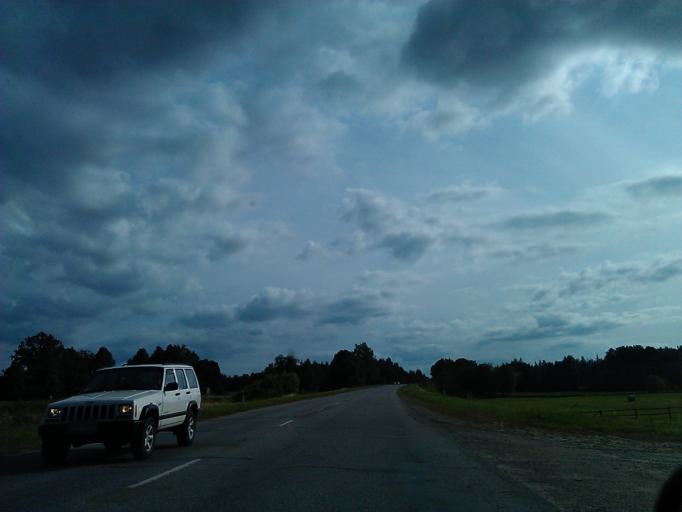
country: LV
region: Cesu Rajons
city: Cesis
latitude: 57.2881
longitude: 25.2996
